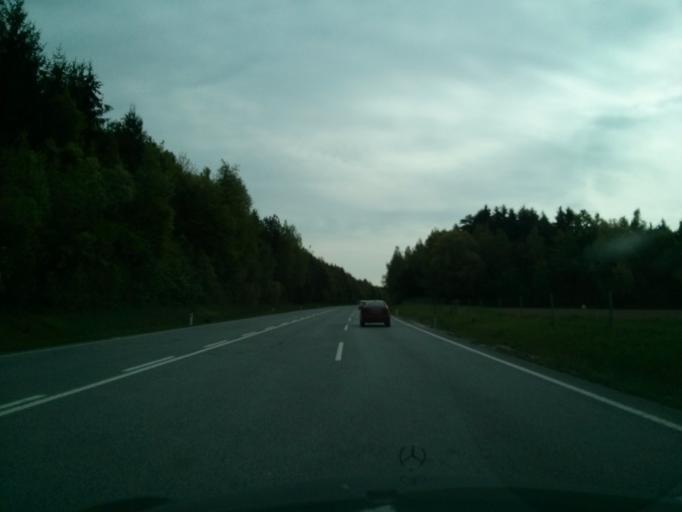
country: AT
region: Burgenland
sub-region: Politischer Bezirk Oberwart
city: Markt Allhau
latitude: 47.2783
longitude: 16.0968
